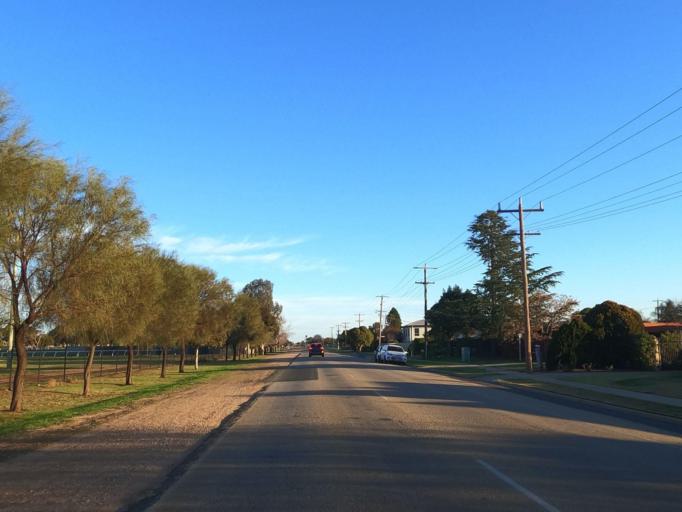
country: AU
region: Victoria
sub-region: Swan Hill
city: Swan Hill
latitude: -35.3514
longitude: 143.5539
